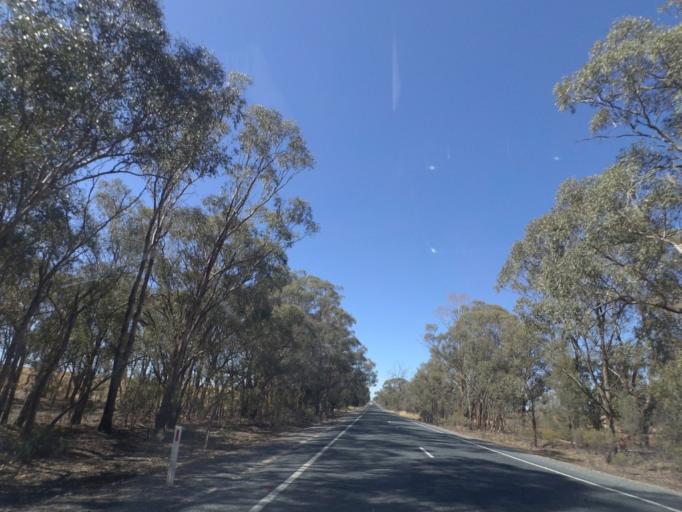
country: AU
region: New South Wales
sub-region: Bland
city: West Wyalong
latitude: -34.1487
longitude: 147.1189
